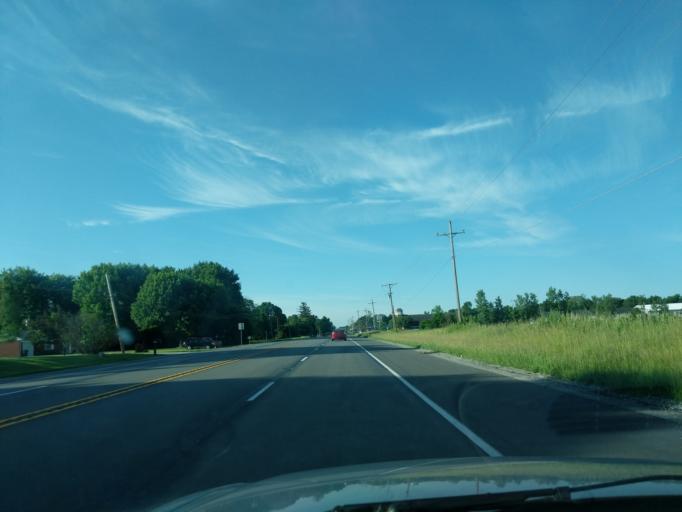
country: US
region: Indiana
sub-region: Madison County
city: Pendleton
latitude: 40.0144
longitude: -85.7301
